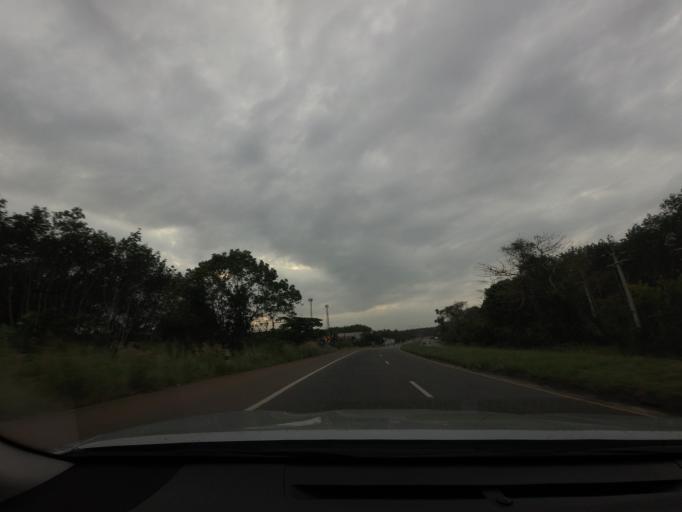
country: TH
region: Surat Thani
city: Phunphin
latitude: 9.0361
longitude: 99.1362
